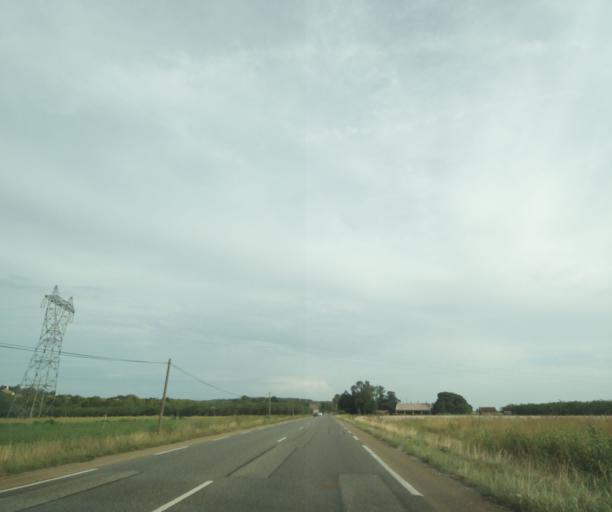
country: FR
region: Midi-Pyrenees
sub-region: Departement du Tarn-et-Garonne
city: Grisolles
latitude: 43.8530
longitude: 1.2802
